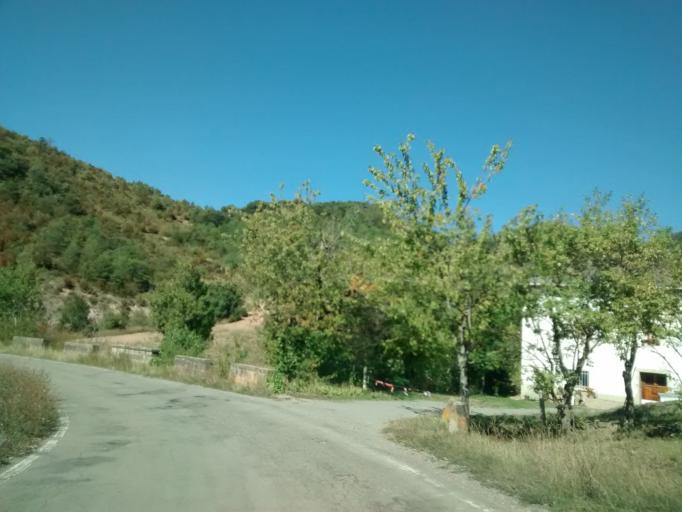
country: ES
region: Aragon
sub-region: Provincia de Huesca
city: Jaca
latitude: 42.4834
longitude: -0.5720
